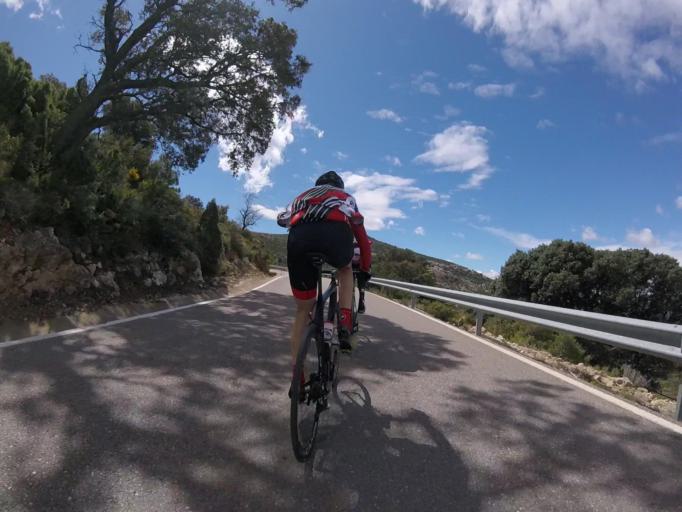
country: ES
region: Valencia
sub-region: Provincia de Castello
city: Sierra-Engarceran
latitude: 40.2855
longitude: -0.0362
